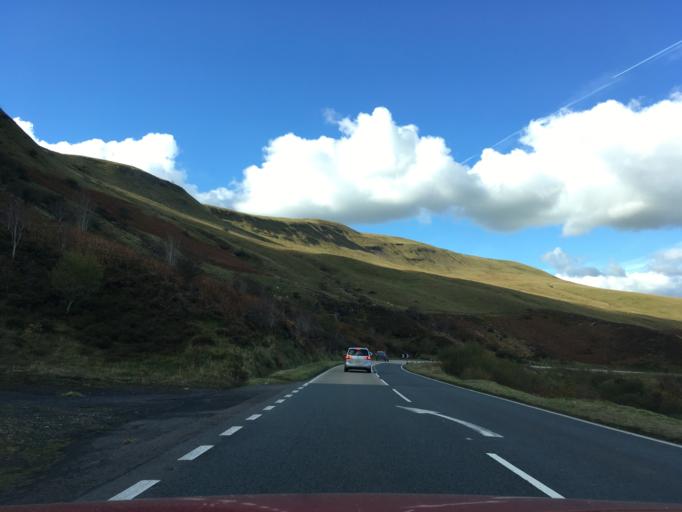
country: GB
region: Wales
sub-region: Sir Powys
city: Cray
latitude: 51.8755
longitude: -3.4942
